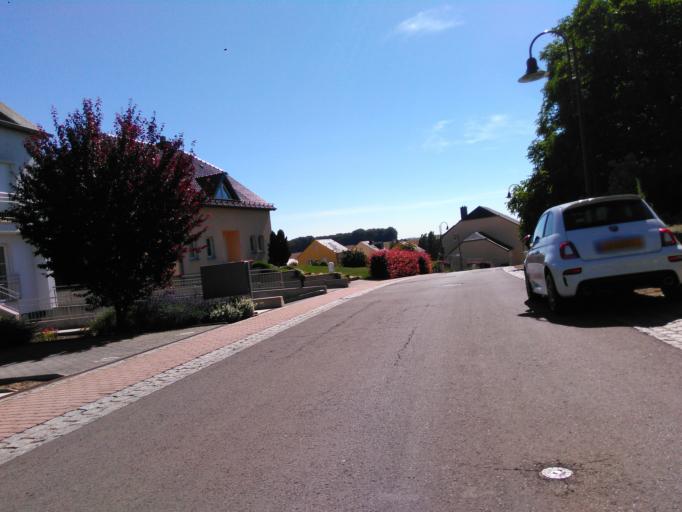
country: LU
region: Luxembourg
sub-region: Canton d'Esch-sur-Alzette
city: Reckange-sur-Mess
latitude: 49.5621
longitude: 6.0099
